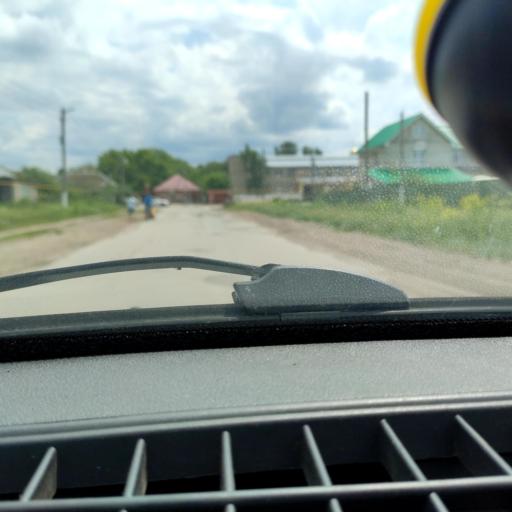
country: RU
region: Samara
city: Povolzhskiy
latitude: 53.6441
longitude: 49.6911
